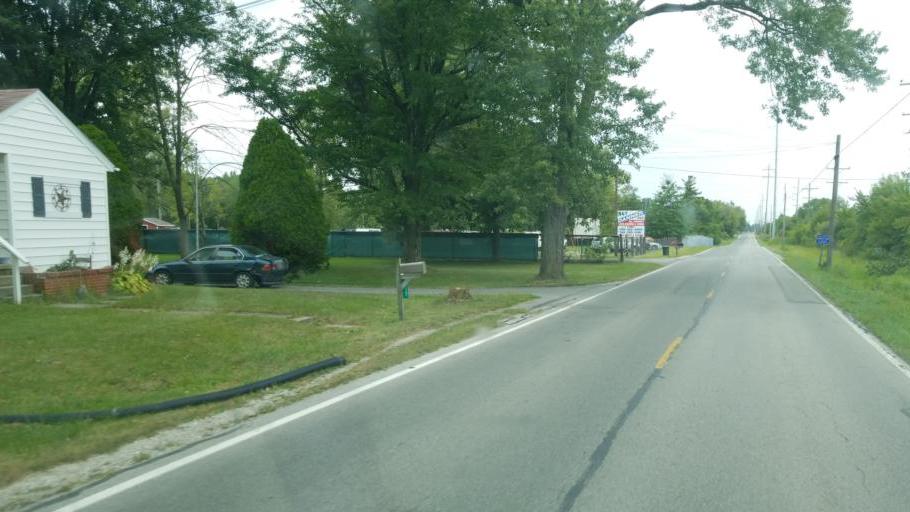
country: US
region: Ohio
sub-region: Marion County
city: Marion
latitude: 40.5563
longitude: -83.1476
